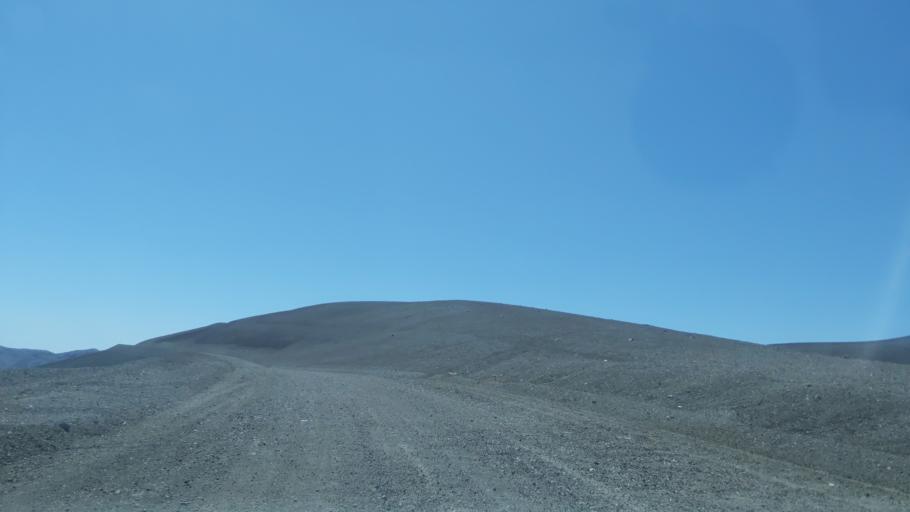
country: CL
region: Araucania
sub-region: Provincia de Cautin
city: Vilcun
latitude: -38.3731
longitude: -71.5389
